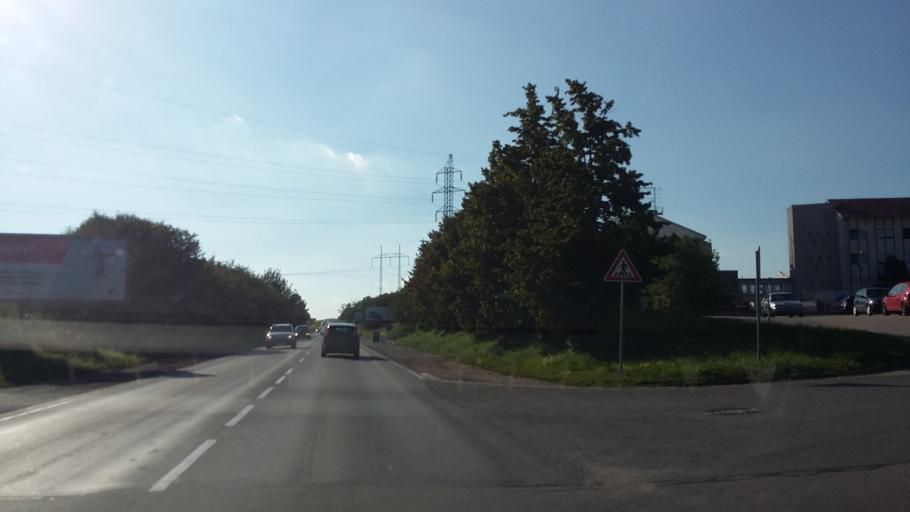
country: CZ
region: South Moravian
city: Troubsko
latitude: 49.1742
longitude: 16.5224
